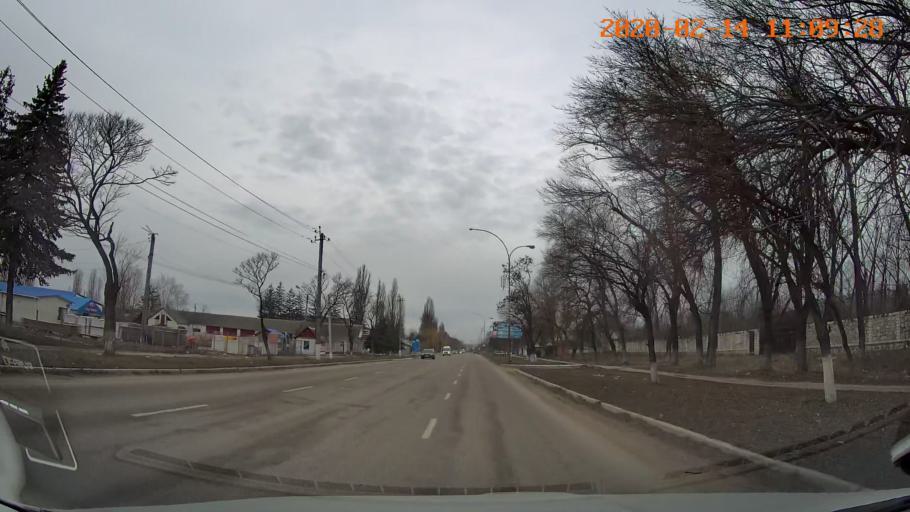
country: MD
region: Raionul Edinet
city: Edinet
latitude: 48.1786
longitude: 27.2938
